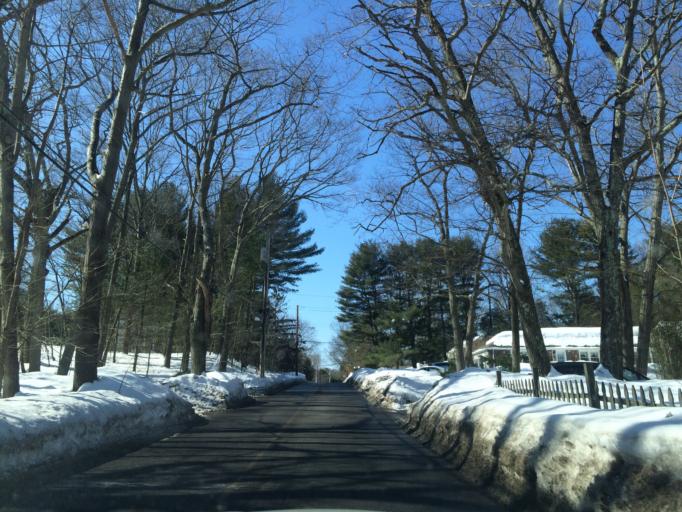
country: US
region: Massachusetts
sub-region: Norfolk County
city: Wellesley
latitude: 42.2946
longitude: -71.3203
